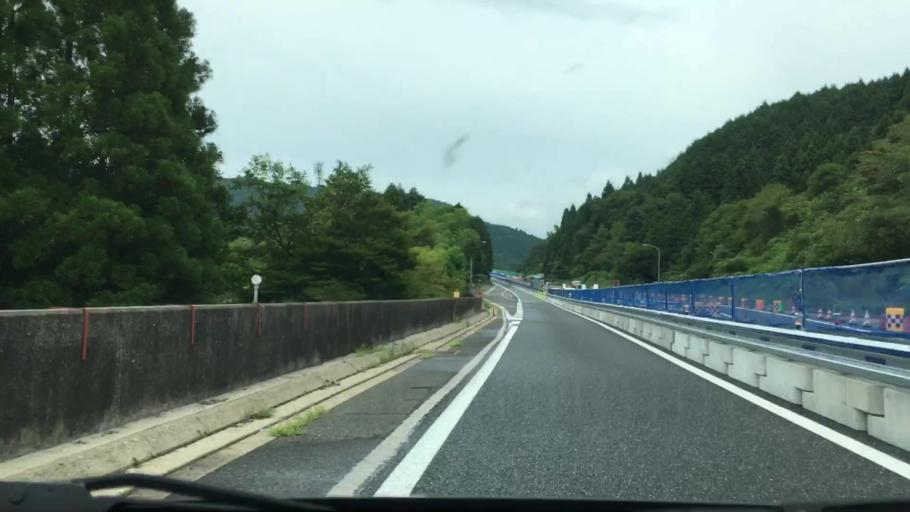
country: JP
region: Okayama
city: Niimi
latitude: 35.0253
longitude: 133.5786
